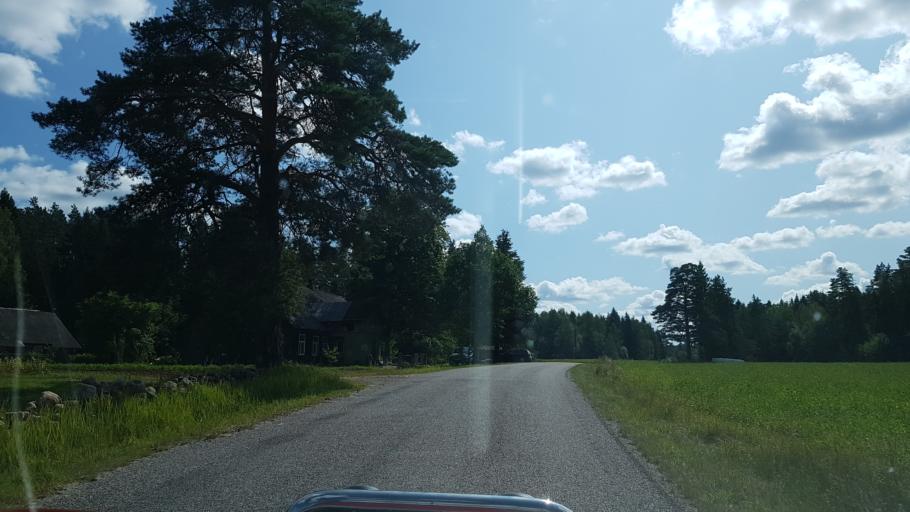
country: EE
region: Vorumaa
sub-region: Voru linn
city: Voru
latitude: 57.7312
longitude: 27.2093
